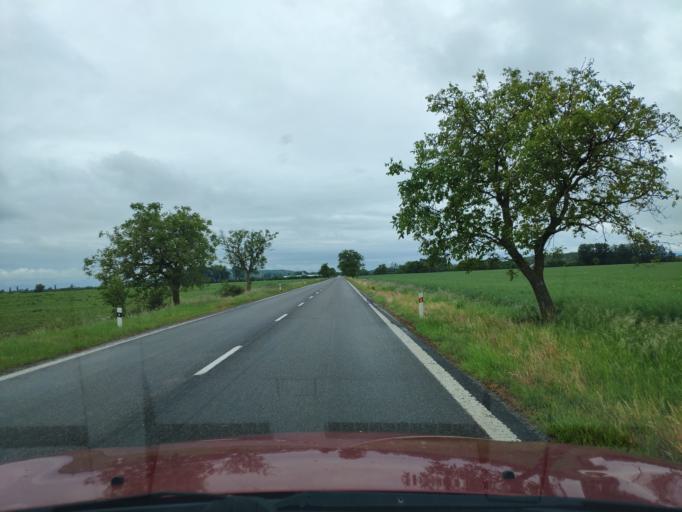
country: HU
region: Borsod-Abauj-Zemplen
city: Karcsa
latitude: 48.4172
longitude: 21.8312
